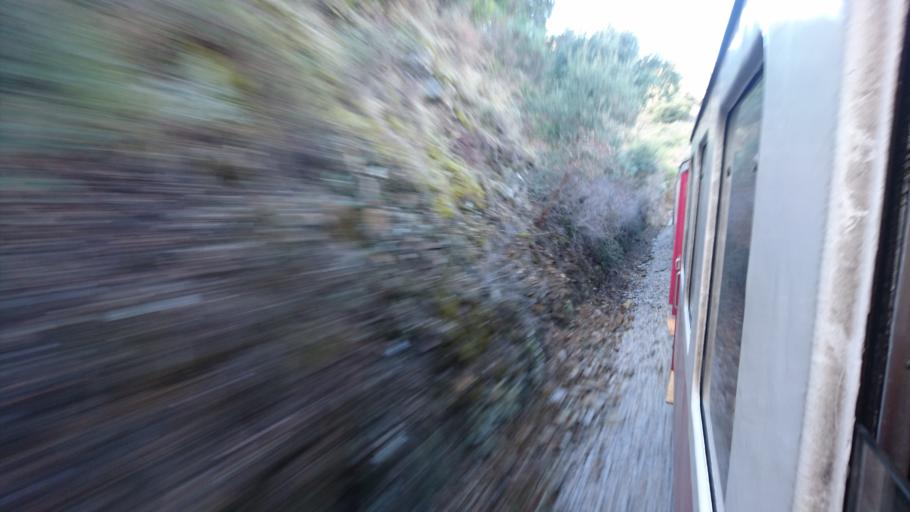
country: PT
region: Guarda
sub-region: Vila Nova de Foz Coa
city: Vila Nova de Foz Coa
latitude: 41.1239
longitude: -7.1847
